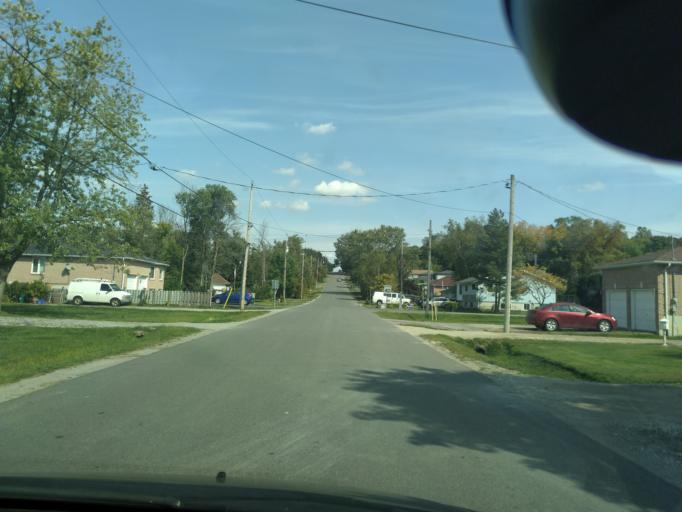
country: CA
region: Ontario
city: Keswick
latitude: 44.1997
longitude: -79.4737
